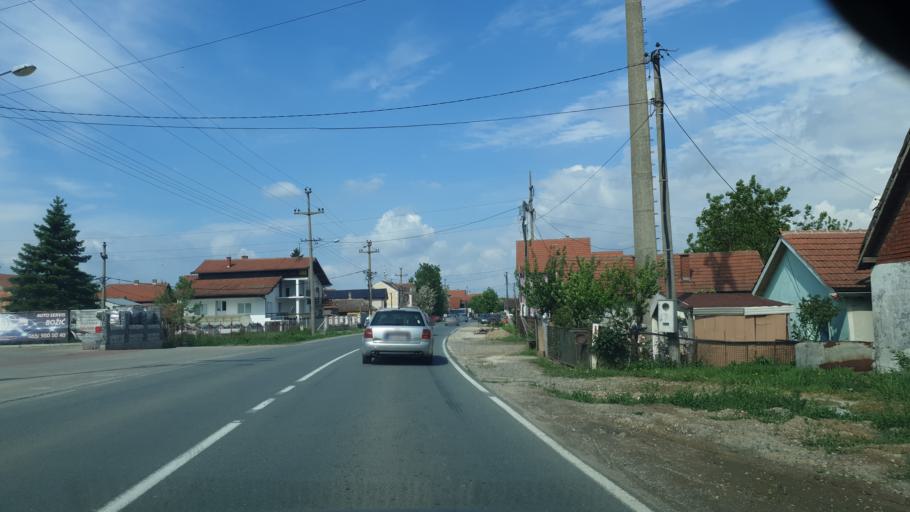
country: RS
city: Zvecka
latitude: 44.6430
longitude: 20.1837
